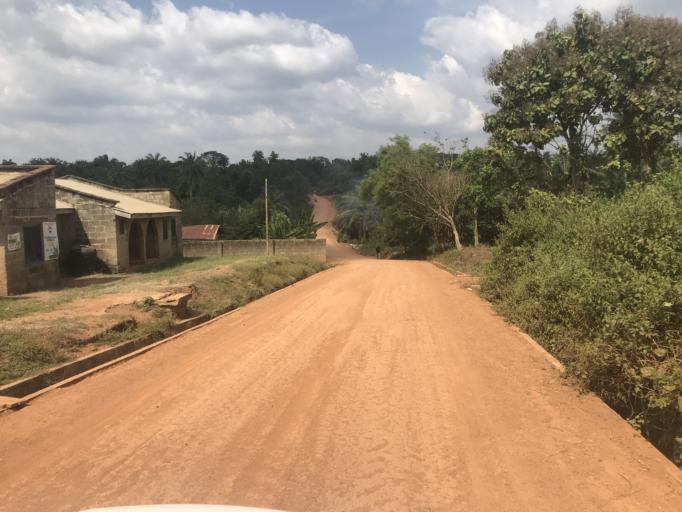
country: NG
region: Osun
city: Inisa
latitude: 7.8563
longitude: 4.3818
